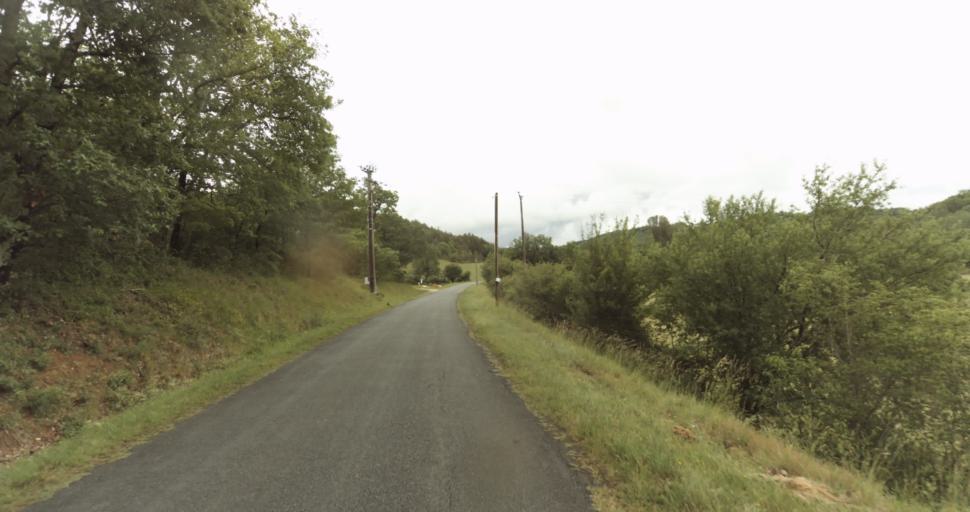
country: FR
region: Aquitaine
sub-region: Departement de la Dordogne
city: Beaumont-du-Perigord
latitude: 44.7526
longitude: 0.8504
